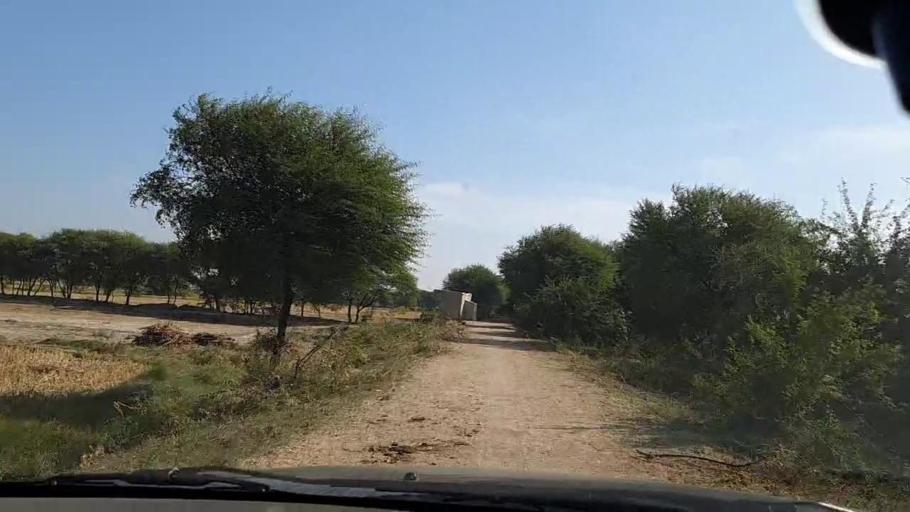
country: PK
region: Sindh
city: Mirpur Batoro
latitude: 24.6313
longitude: 68.2643
